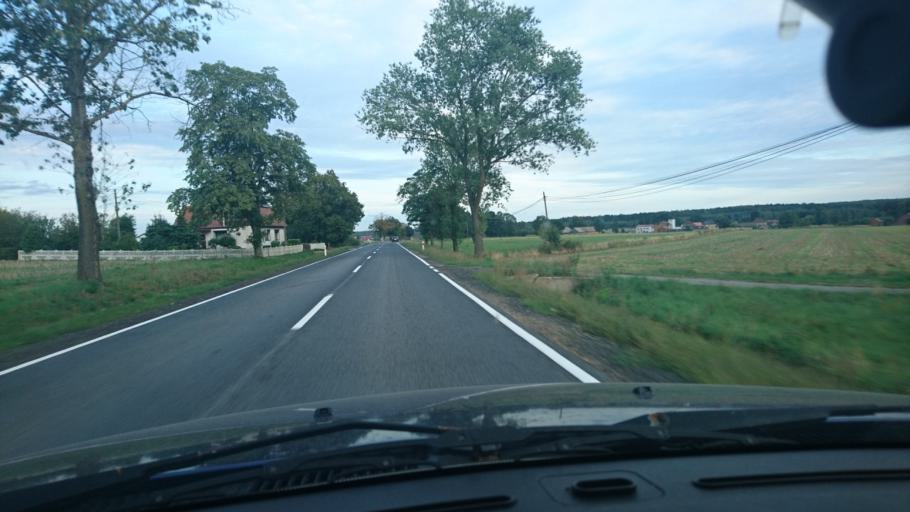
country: PL
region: Silesian Voivodeship
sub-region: Powiat lubliniecki
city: Sierakow Slaski
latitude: 50.8304
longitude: 18.5221
